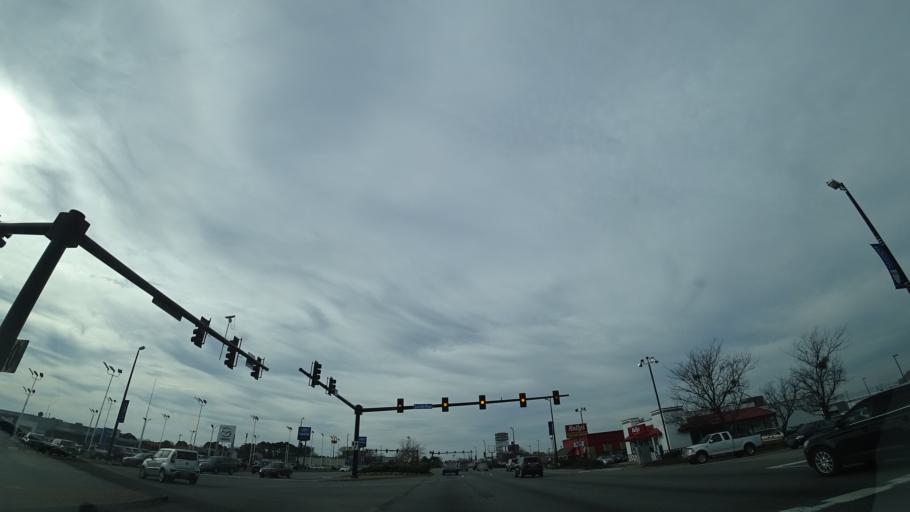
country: US
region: Virginia
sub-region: City of Hampton
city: Hampton
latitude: 37.0427
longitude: -76.3837
